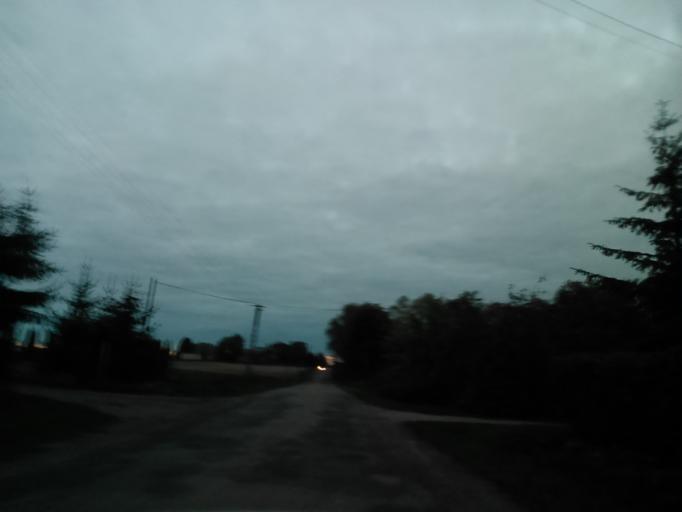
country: PL
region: Kujawsko-Pomorskie
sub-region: Powiat golubsko-dobrzynski
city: Kowalewo Pomorskie
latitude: 53.1141
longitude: 18.8937
